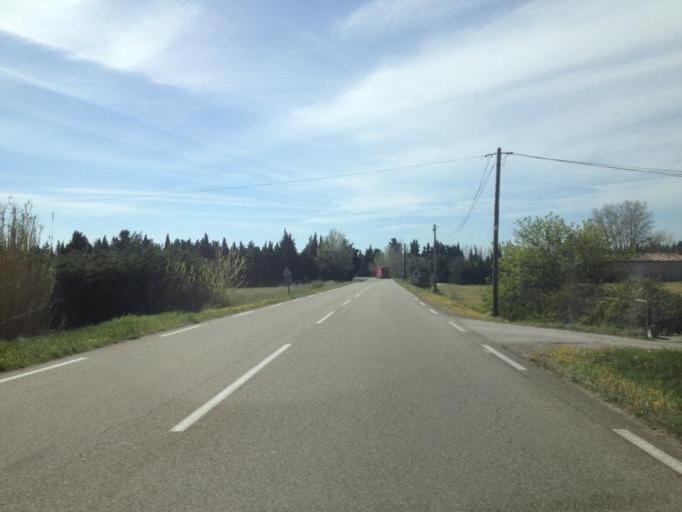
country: FR
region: Provence-Alpes-Cote d'Azur
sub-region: Departement du Vaucluse
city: Orange
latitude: 44.1362
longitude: 4.7818
